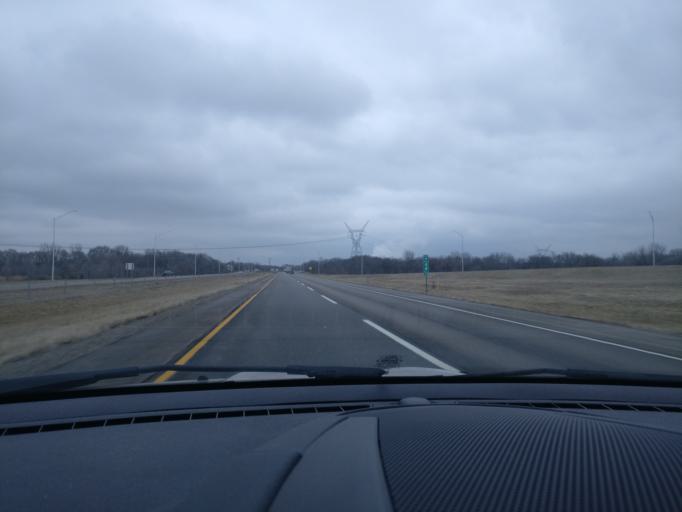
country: US
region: Illinois
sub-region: Whiteside County
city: Rock Falls
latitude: 41.7585
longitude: -89.6365
